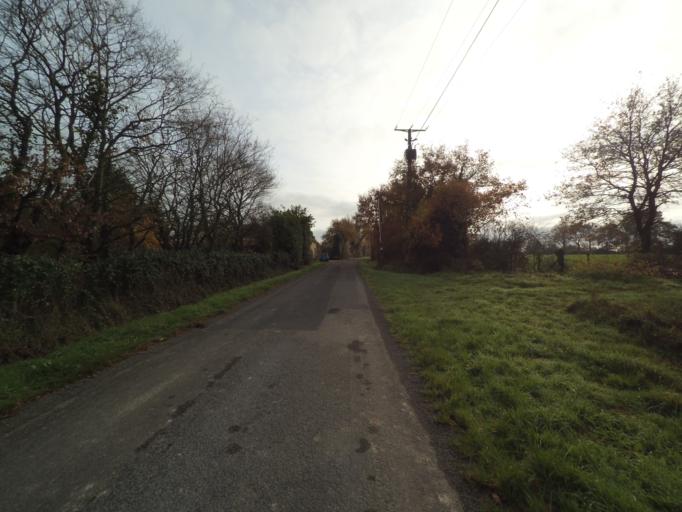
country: FR
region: Pays de la Loire
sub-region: Departement de la Loire-Atlantique
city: La Planche
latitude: 47.0223
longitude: -1.4055
